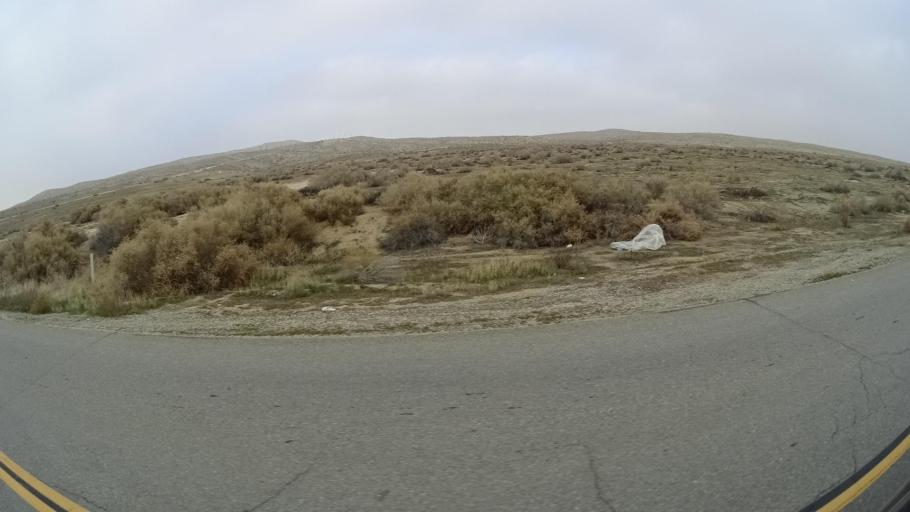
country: US
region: California
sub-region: Kern County
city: Maricopa
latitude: 35.1301
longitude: -119.3748
